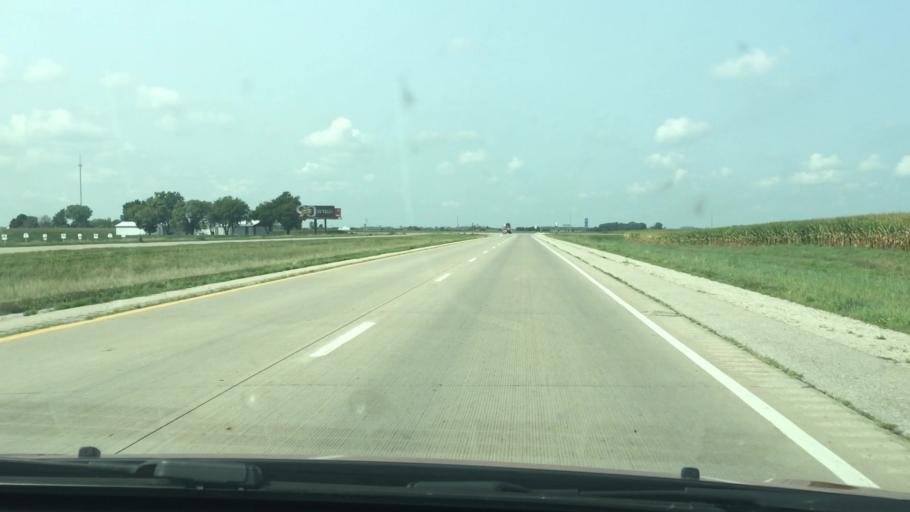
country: US
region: Iowa
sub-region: Muscatine County
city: Wilton
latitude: 41.4990
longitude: -90.9655
